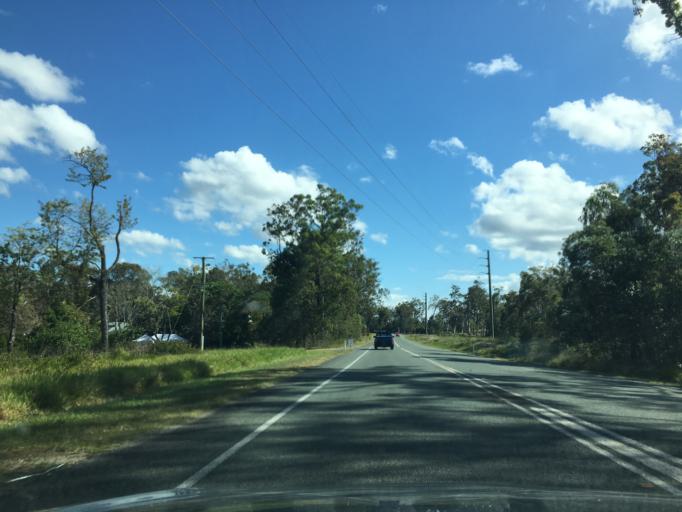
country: AU
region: Queensland
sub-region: Logan
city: Chambers Flat
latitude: -27.7794
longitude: 153.1009
